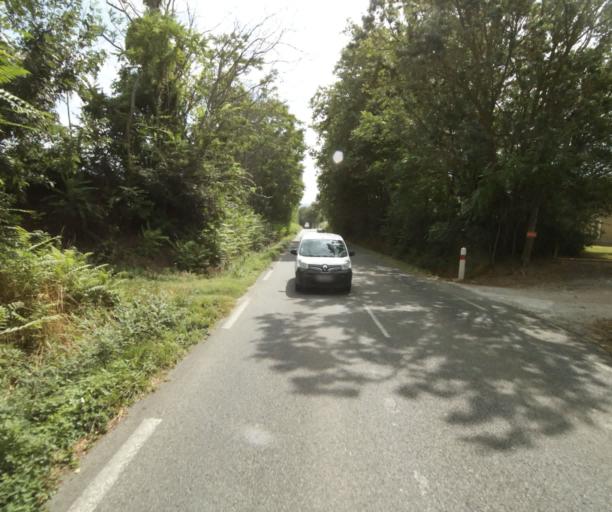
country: FR
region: Midi-Pyrenees
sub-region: Departement de la Haute-Garonne
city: Saint-Felix-Lauragais
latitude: 43.4498
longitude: 1.9071
